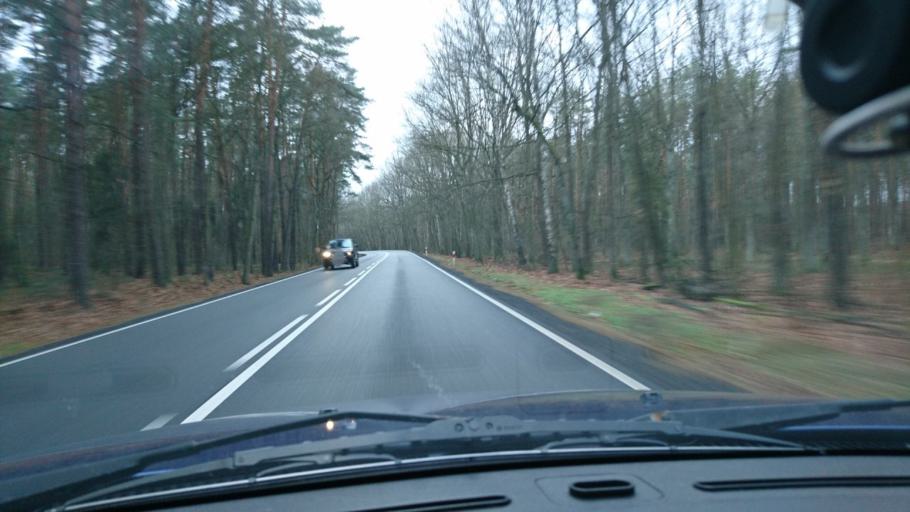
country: PL
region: Opole Voivodeship
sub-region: Powiat kluczborski
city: Kluczbork
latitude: 50.9439
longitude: 18.3222
